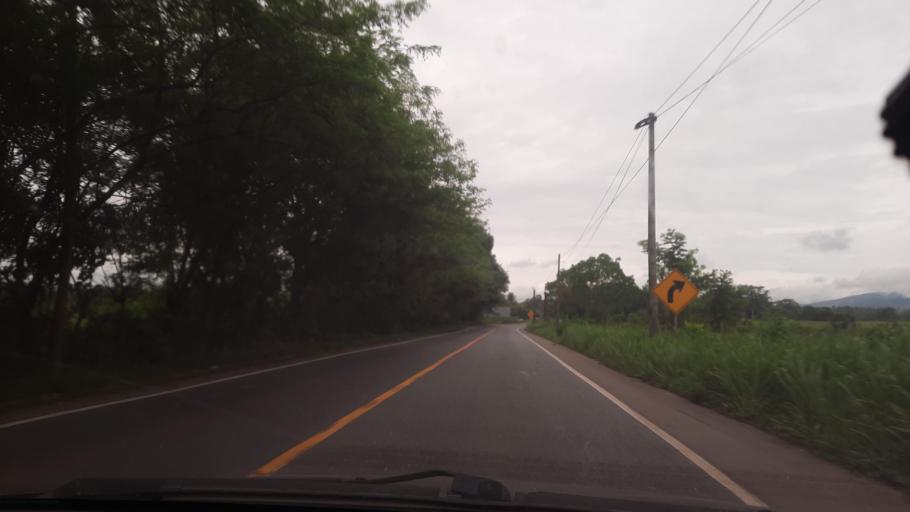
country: GT
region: Izabal
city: Morales
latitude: 15.4521
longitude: -88.9365
